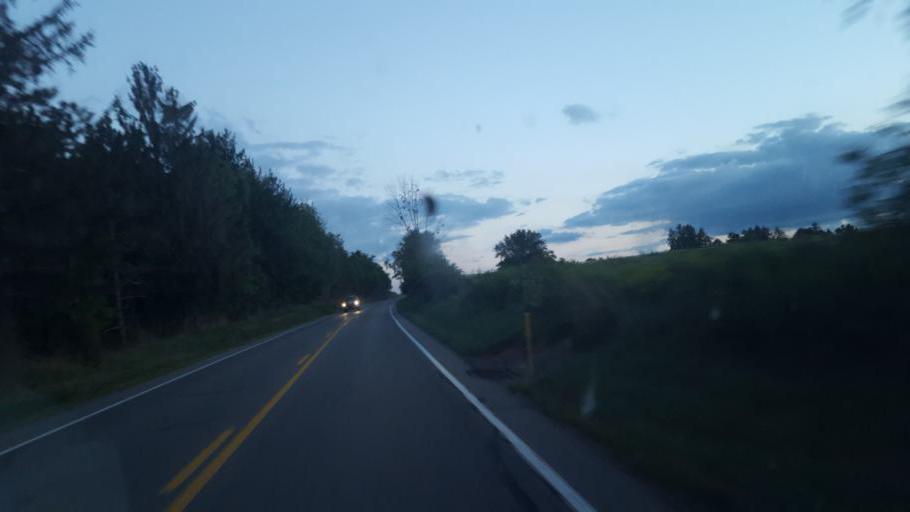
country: US
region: Pennsylvania
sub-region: Clarion County
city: Knox
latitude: 41.1996
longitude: -79.5442
